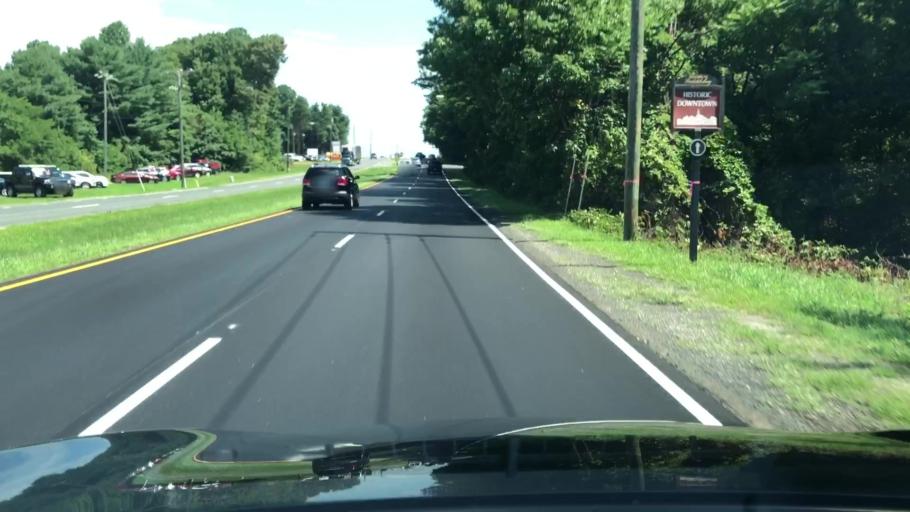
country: US
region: Virginia
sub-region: City of Fredericksburg
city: Fredericksburg
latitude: 38.2759
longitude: -77.4910
